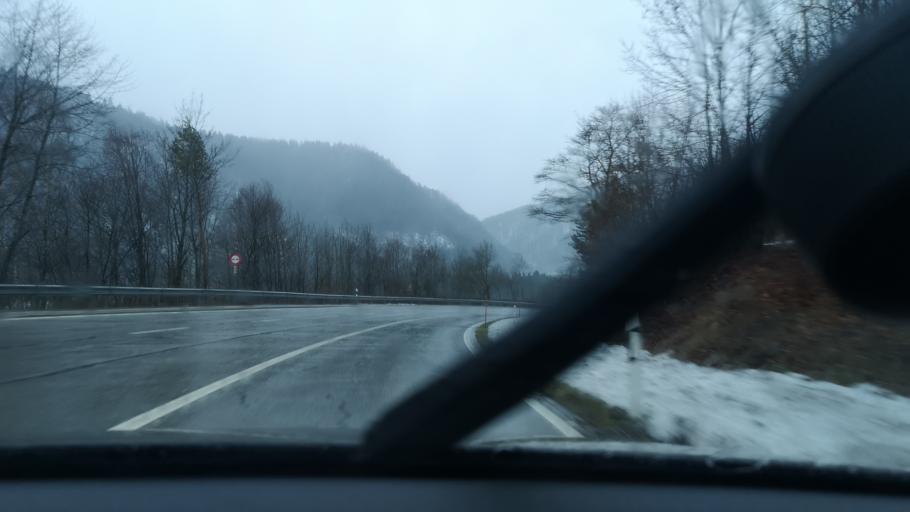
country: CH
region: Neuchatel
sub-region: Le Locle District
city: Les Ponts-de-Martel
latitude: 46.9567
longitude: 6.7214
